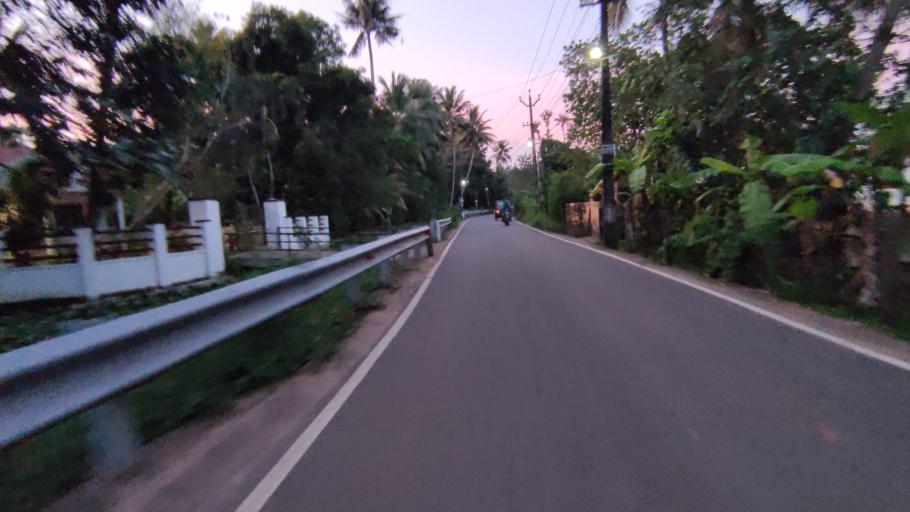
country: IN
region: Kerala
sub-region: Kottayam
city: Kottayam
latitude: 9.5841
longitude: 76.4361
